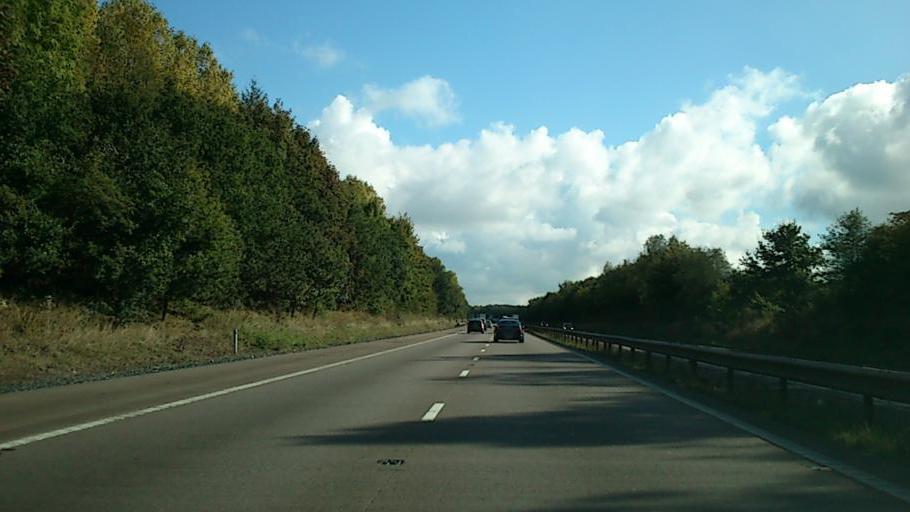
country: GB
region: England
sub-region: Shropshire
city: Albrighton
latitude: 52.6514
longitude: -2.2607
